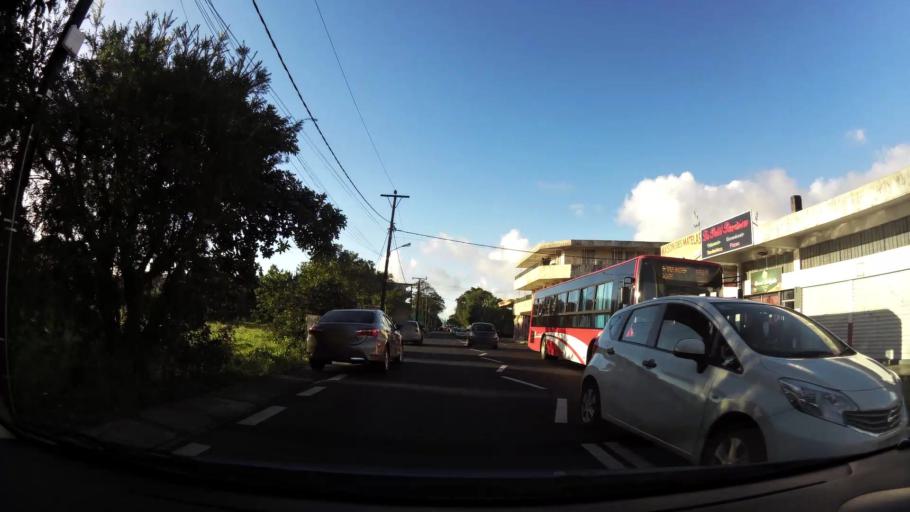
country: MU
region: Plaines Wilhems
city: Curepipe
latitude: -20.3110
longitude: 57.5243
